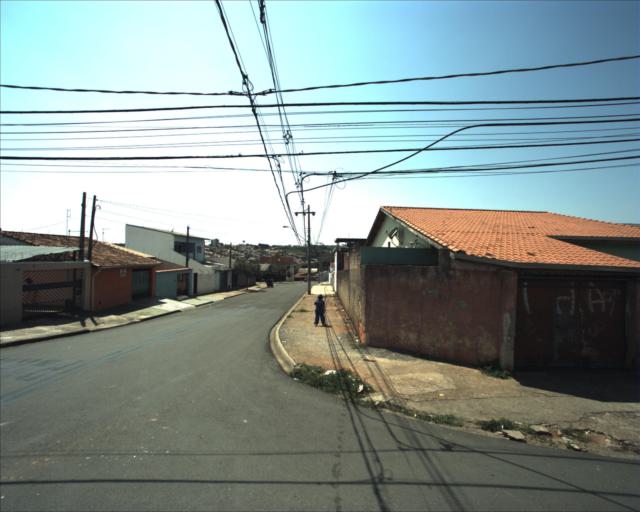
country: BR
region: Sao Paulo
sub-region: Sorocaba
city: Sorocaba
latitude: -23.4620
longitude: -47.4926
